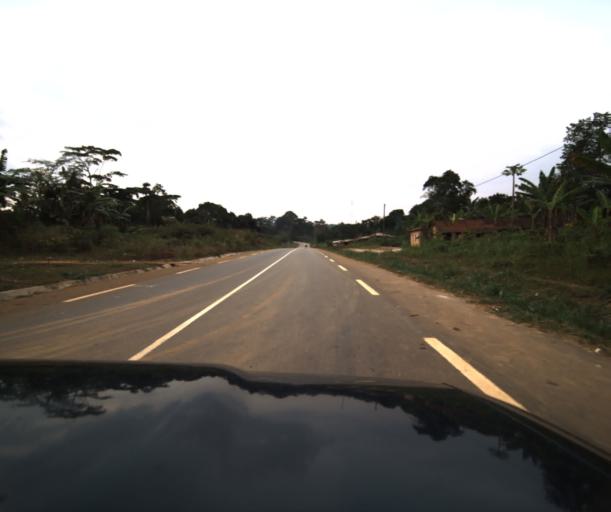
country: CM
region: Centre
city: Mbankomo
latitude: 3.7445
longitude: 11.3998
